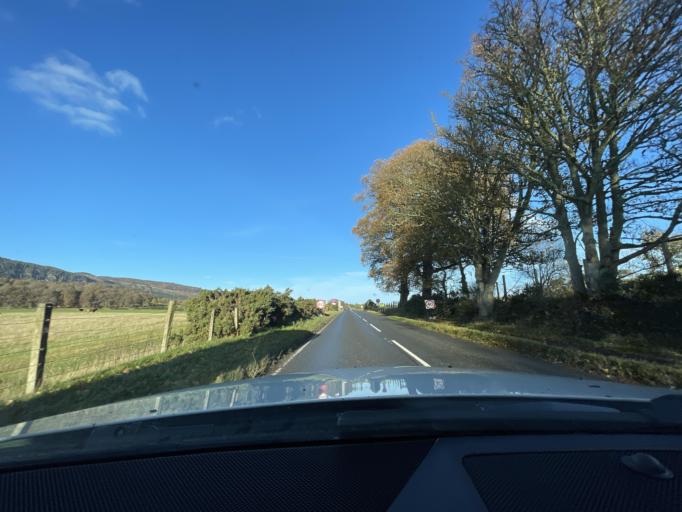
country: GB
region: Scotland
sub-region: Highland
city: Inverness
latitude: 57.3860
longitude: -4.3288
